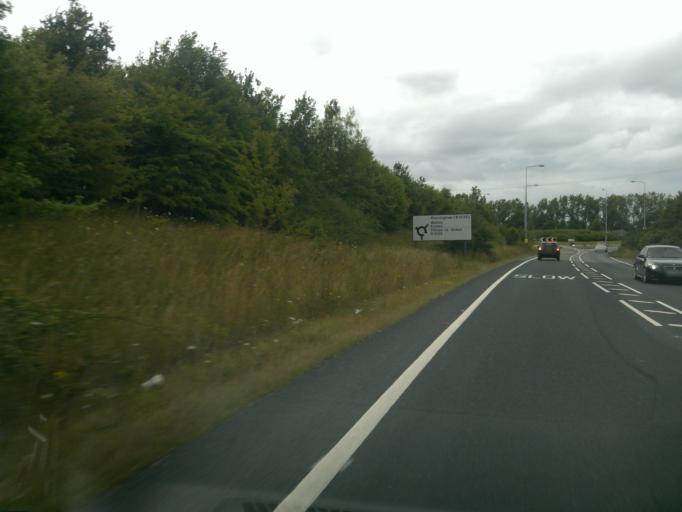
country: GB
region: England
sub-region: Essex
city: Great Bentley
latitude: 51.8580
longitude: 1.1010
